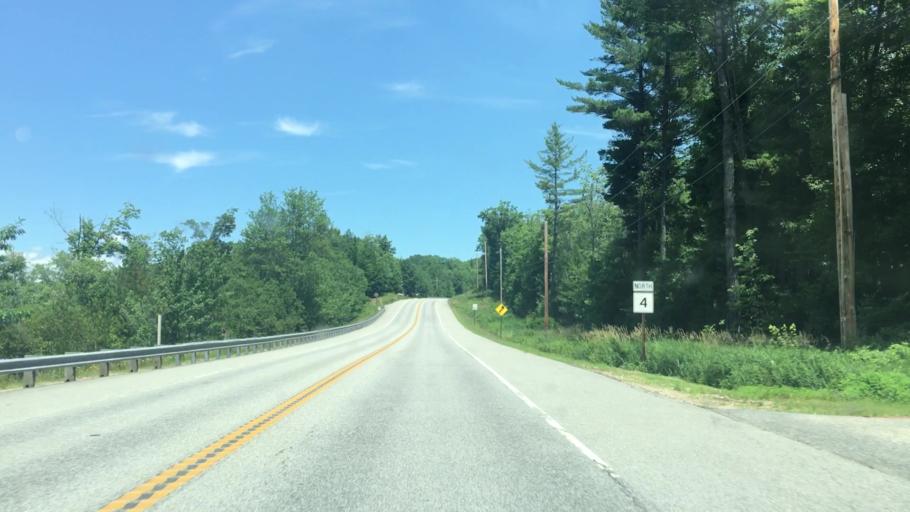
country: US
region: Maine
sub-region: Androscoggin County
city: Livermore
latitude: 44.4095
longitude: -70.2234
